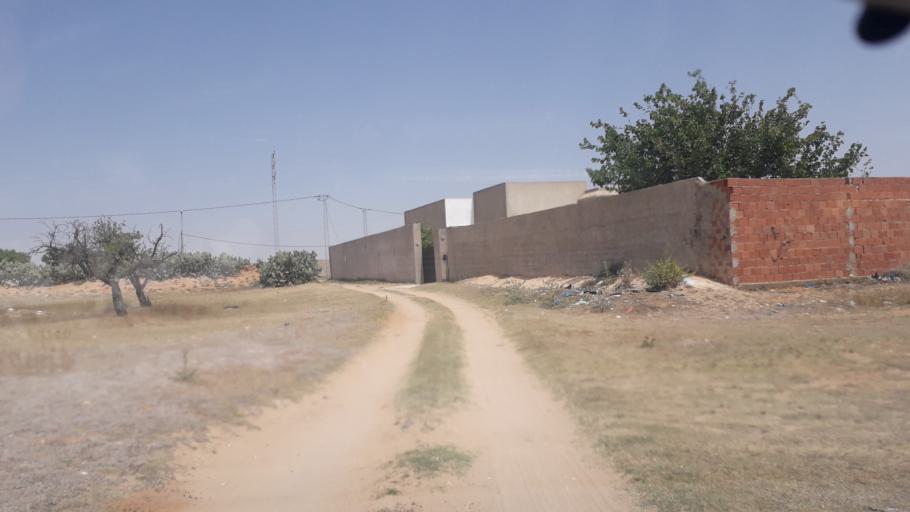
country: TN
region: Safaqis
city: Al Qarmadah
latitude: 34.8371
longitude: 10.7693
